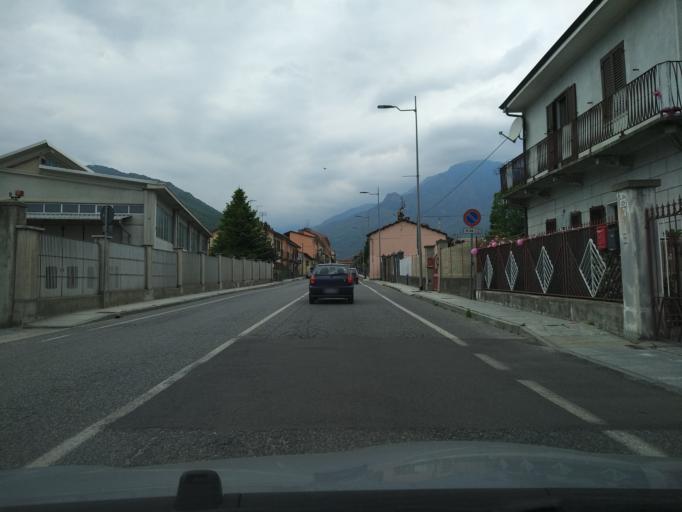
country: IT
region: Piedmont
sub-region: Provincia di Torino
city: Airali
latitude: 44.8130
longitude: 7.2534
